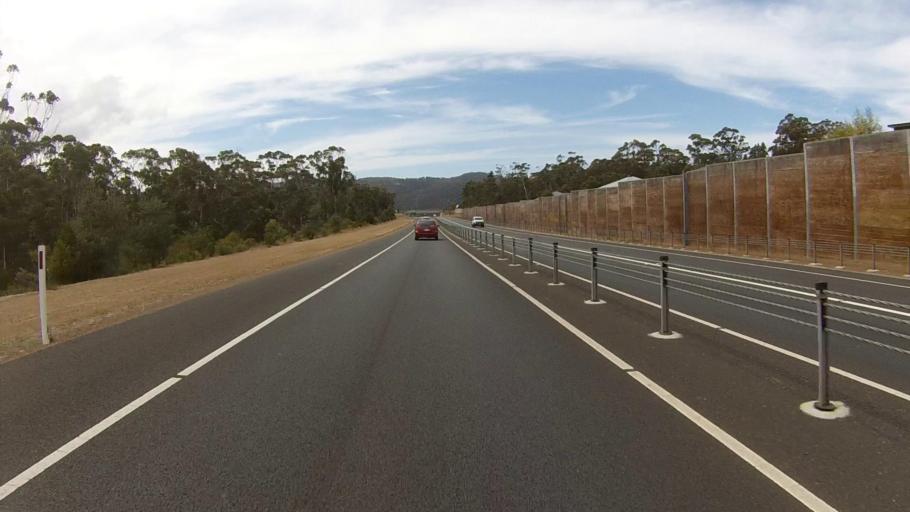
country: AU
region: Tasmania
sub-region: Kingborough
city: Kingston
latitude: -42.9792
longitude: 147.2955
